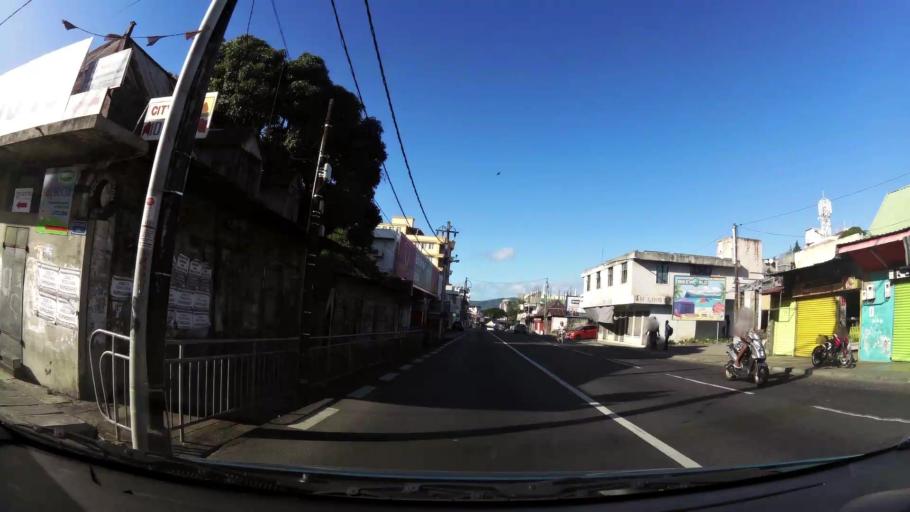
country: MU
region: Port Louis
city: Port Louis
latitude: -20.1663
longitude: 57.4894
